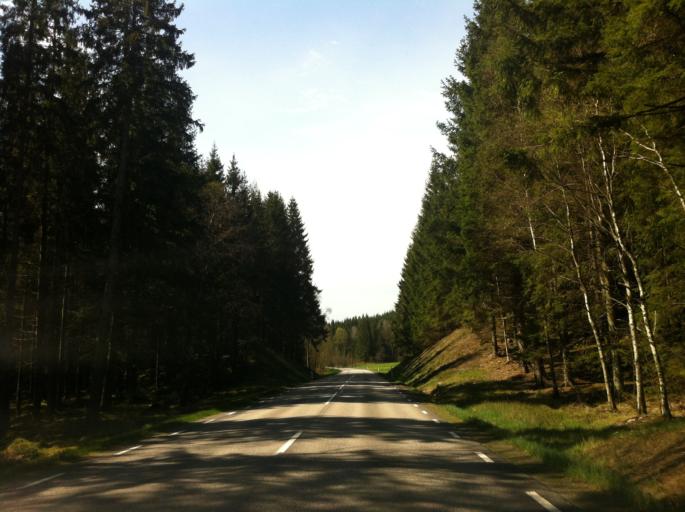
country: SE
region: Vaestra Goetaland
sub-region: Marks Kommun
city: Kinna
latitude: 57.1797
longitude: 12.7752
